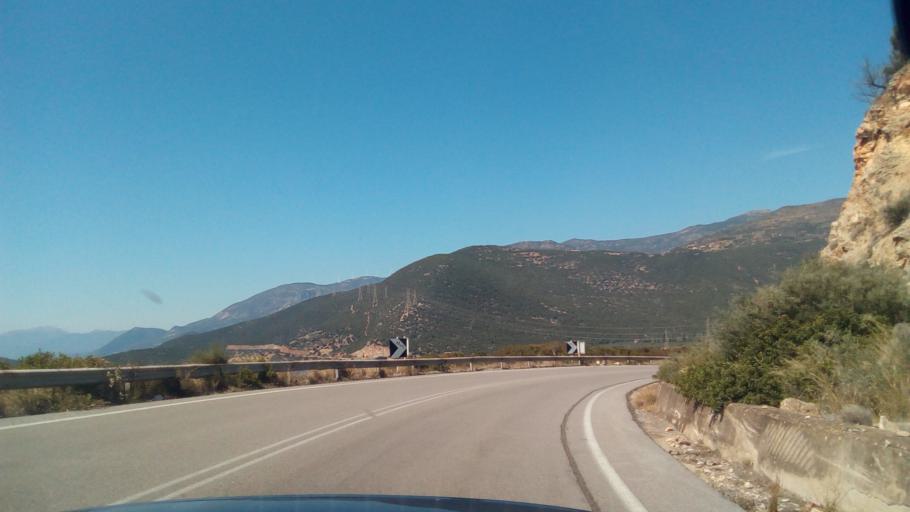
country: GR
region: West Greece
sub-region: Nomos Achaias
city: Aigio
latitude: 38.3600
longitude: 22.1285
